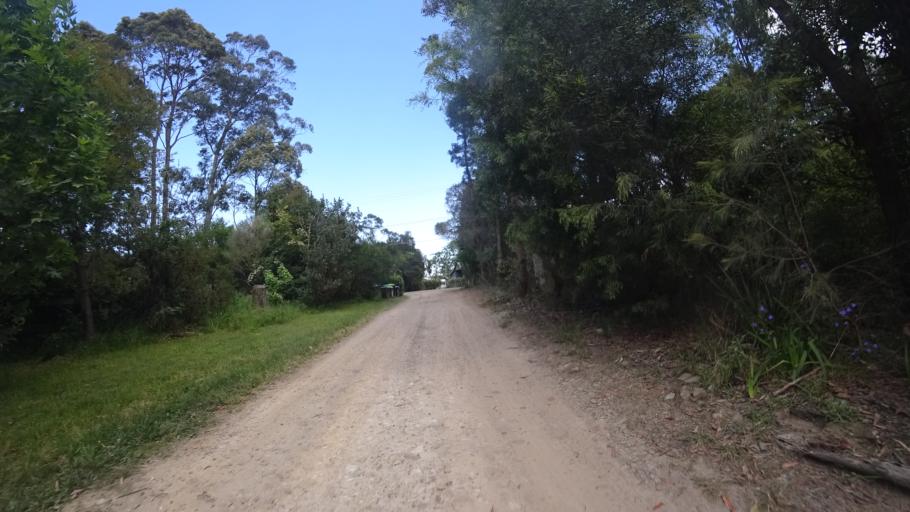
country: AU
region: New South Wales
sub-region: City of Sydney
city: North Turramurra
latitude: -33.6780
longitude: 151.1910
